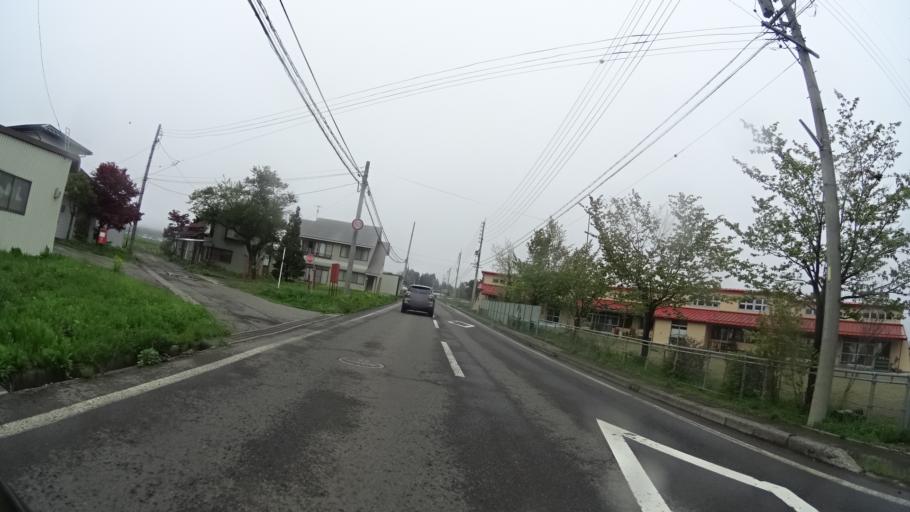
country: JP
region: Nagano
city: Nagano-shi
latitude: 36.7751
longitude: 138.2023
